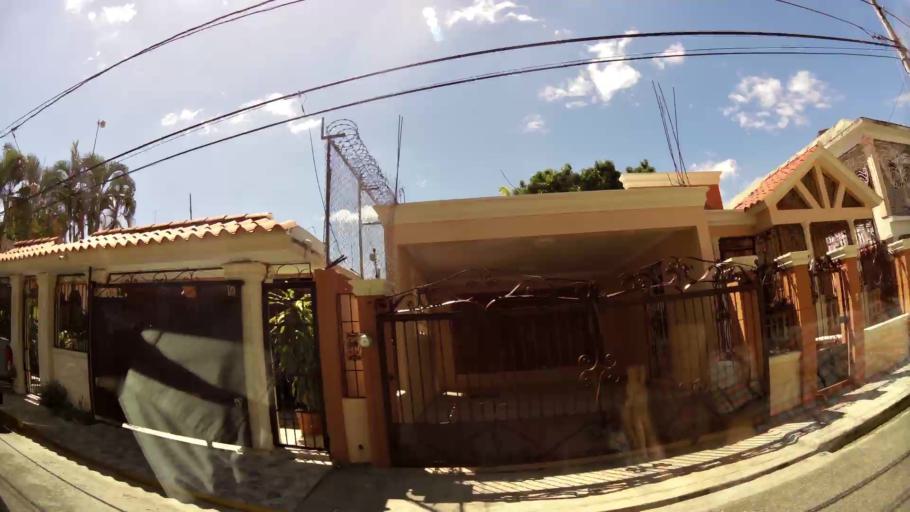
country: DO
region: San Cristobal
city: San Cristobal
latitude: 18.4166
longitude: -70.0917
